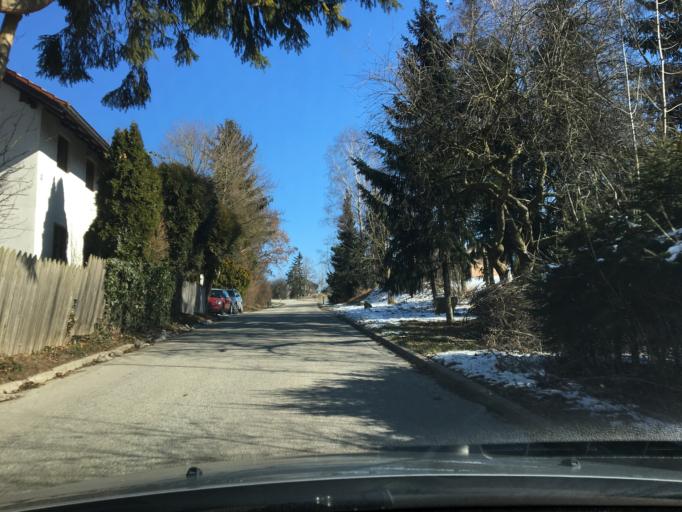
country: DE
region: Bavaria
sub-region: Lower Bavaria
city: Tiefenbach
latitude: 48.4769
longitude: 12.0918
